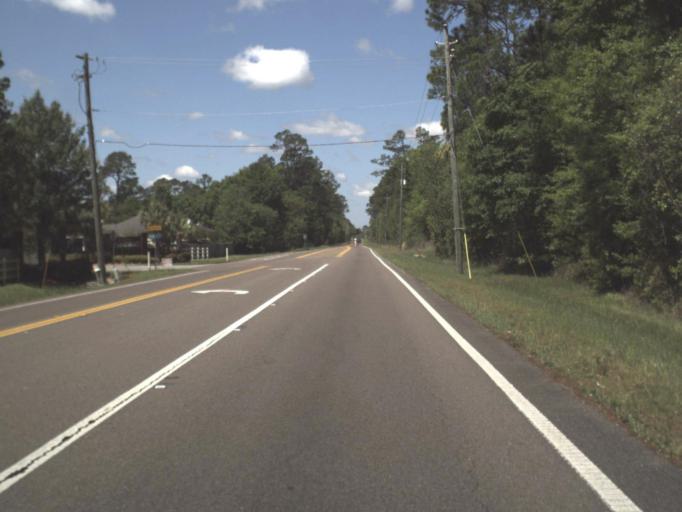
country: US
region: Florida
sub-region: Escambia County
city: Myrtle Grove
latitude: 30.4220
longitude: -87.3317
